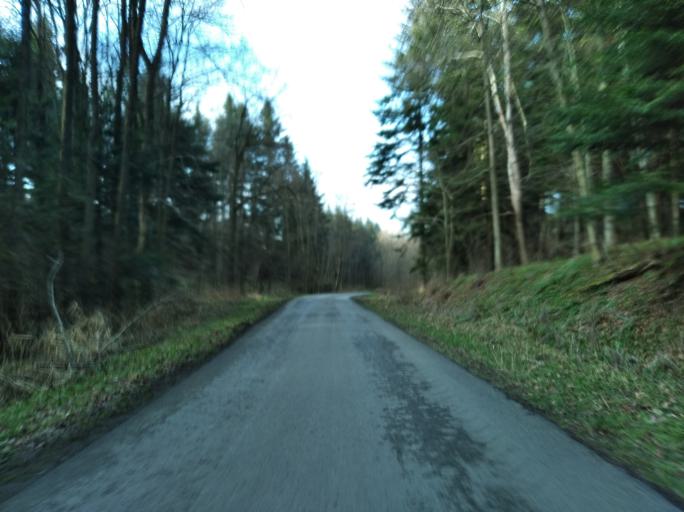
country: PL
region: Subcarpathian Voivodeship
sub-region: Powiat strzyzowski
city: Konieczkowa
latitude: 49.8276
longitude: 21.9407
